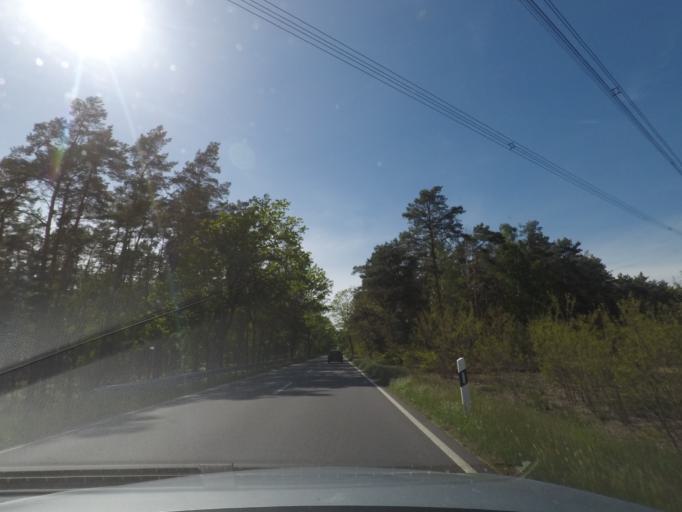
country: DE
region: Brandenburg
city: Luebben
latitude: 51.9474
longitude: 13.8073
